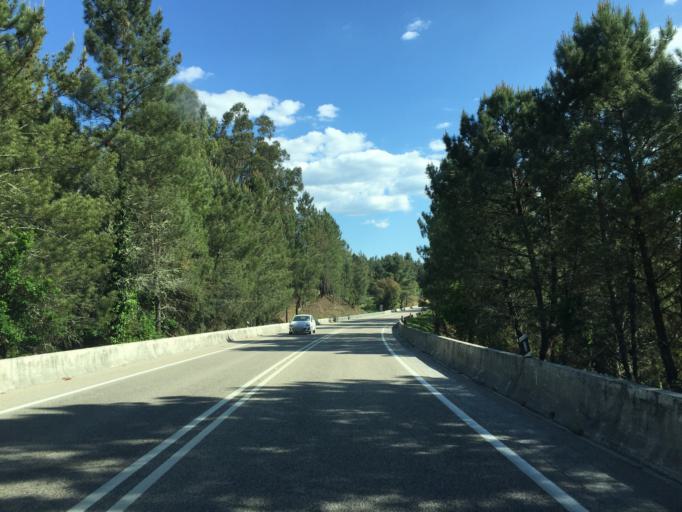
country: PT
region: Leiria
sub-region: Pedrogao Grande
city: Pedrogao Grande
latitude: 39.9196
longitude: -8.1541
